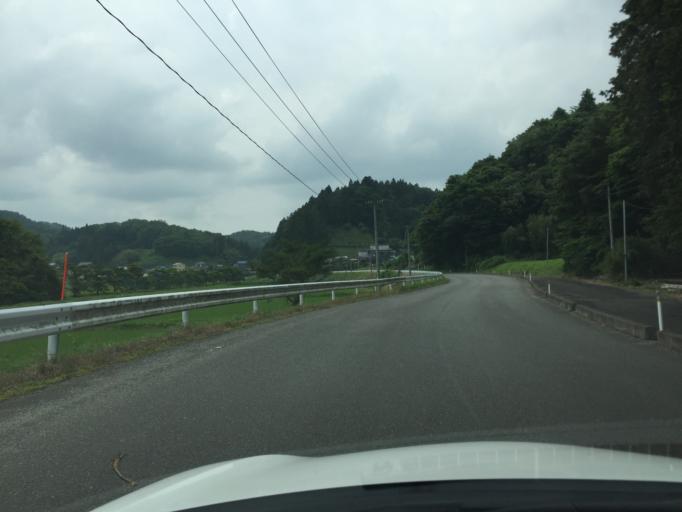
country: JP
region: Fukushima
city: Funehikimachi-funehiki
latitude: 37.2933
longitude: 140.5820
